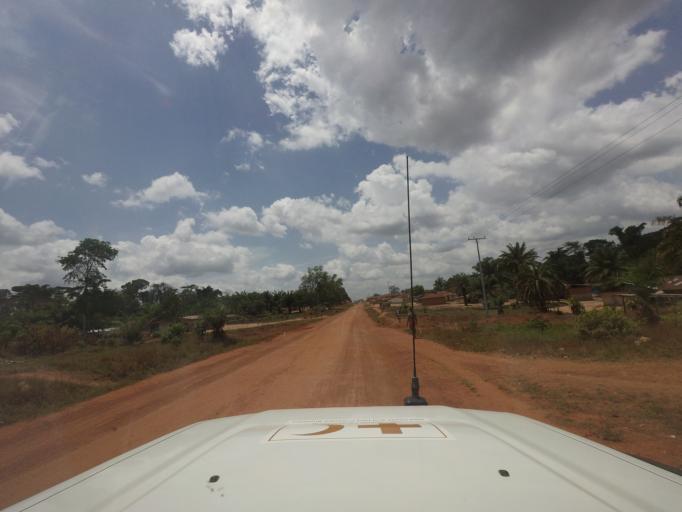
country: LR
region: Nimba
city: Sanniquellie
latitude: 7.2263
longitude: -8.9326
